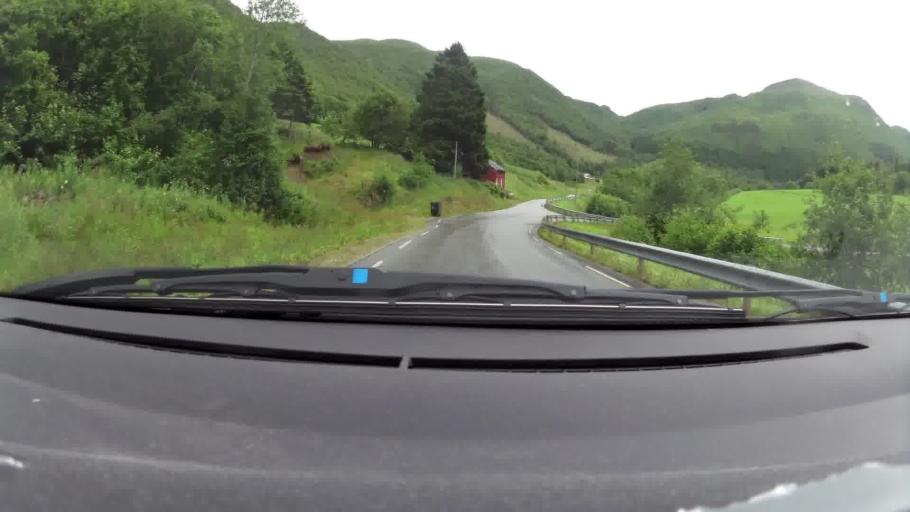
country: NO
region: More og Romsdal
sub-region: Gjemnes
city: Batnfjordsora
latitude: 62.9043
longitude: 7.7839
